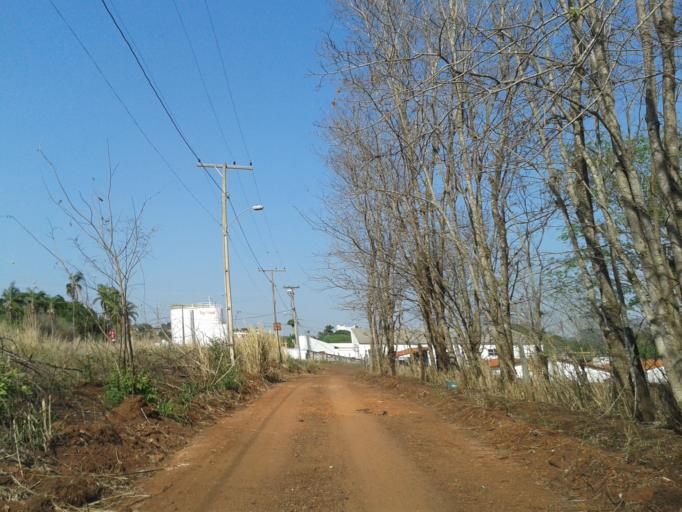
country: BR
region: Minas Gerais
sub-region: Ituiutaba
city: Ituiutaba
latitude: -18.9440
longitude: -49.4542
